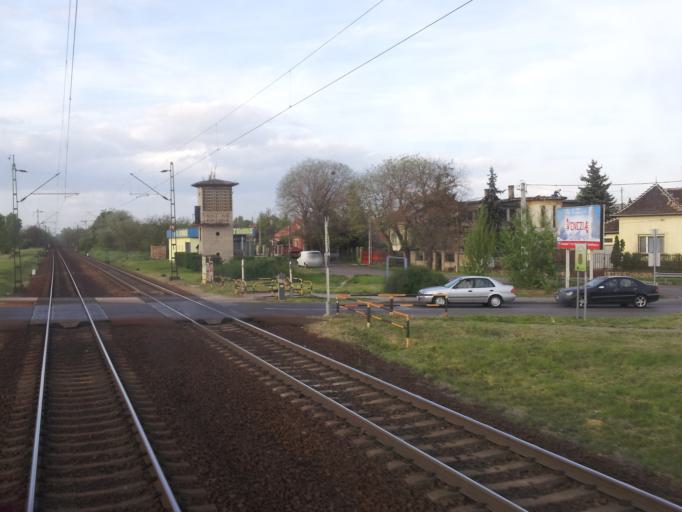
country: HU
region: Budapest
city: Budapest XV. keruelet
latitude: 47.5760
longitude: 19.1164
